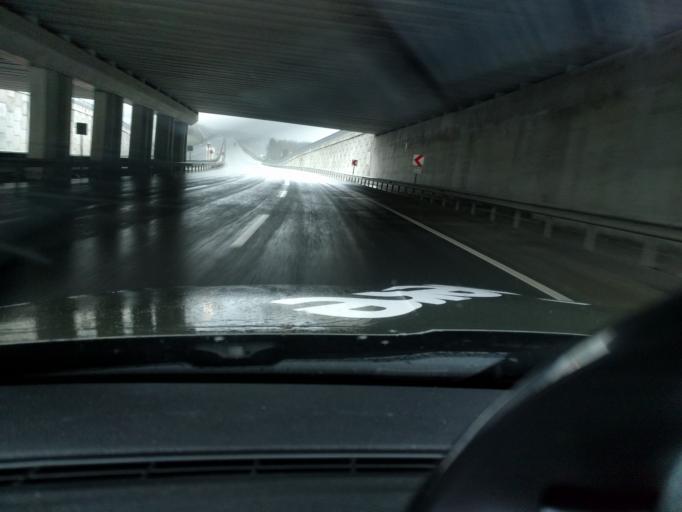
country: TR
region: Istanbul
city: Boyalik
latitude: 41.2355
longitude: 28.5558
